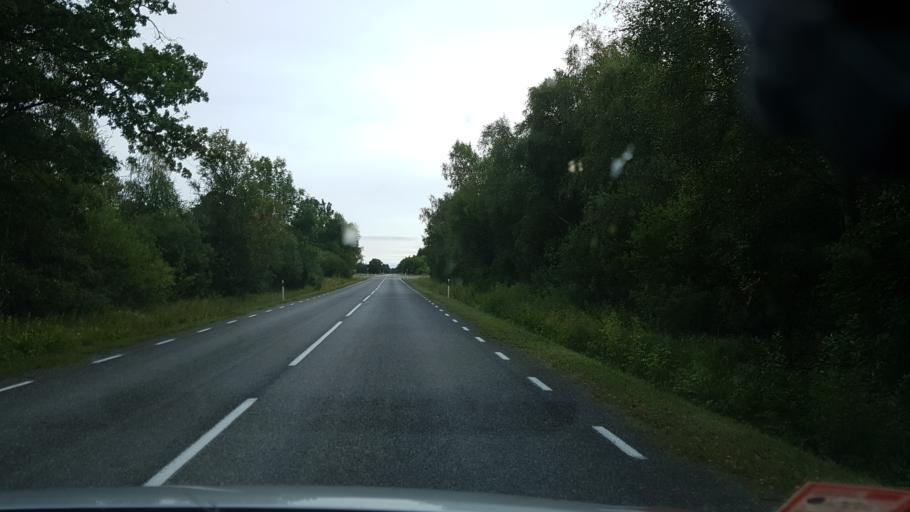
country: EE
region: Saare
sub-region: Kuressaare linn
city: Kuressaare
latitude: 58.3659
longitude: 22.0534
